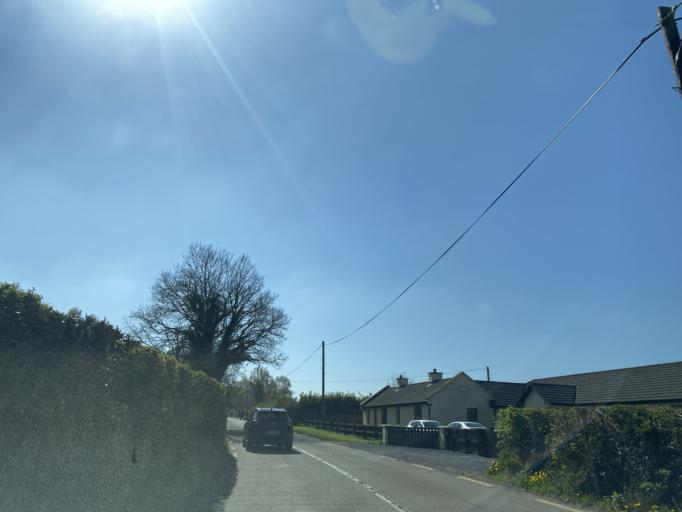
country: IE
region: Leinster
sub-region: Kildare
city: Kill
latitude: 53.2700
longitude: -6.5883
